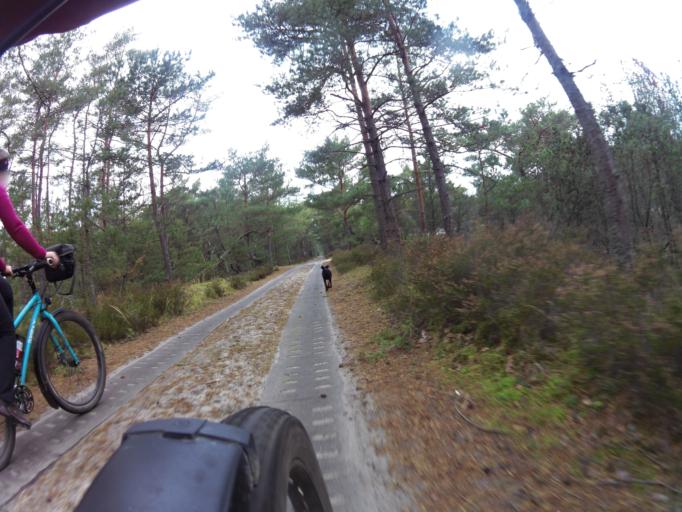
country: PL
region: Pomeranian Voivodeship
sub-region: Powiat pucki
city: Hel
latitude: 54.6239
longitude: 18.8177
